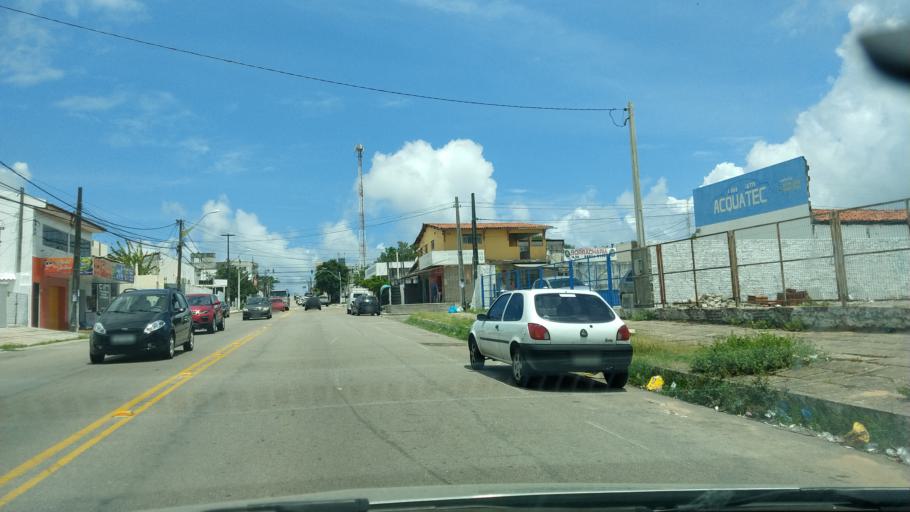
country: BR
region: Rio Grande do Norte
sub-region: Natal
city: Natal
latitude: -5.8185
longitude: -35.2009
